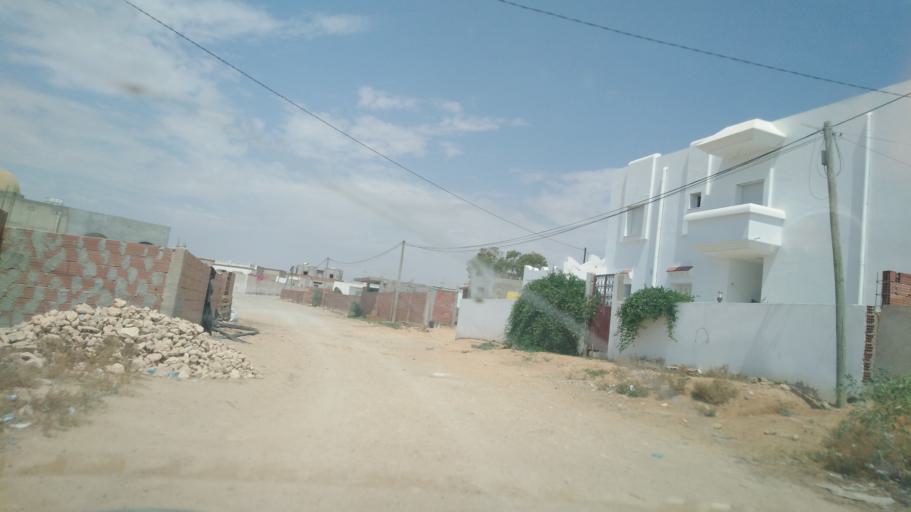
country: TN
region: Safaqis
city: Sfax
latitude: 34.7425
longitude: 10.5611
